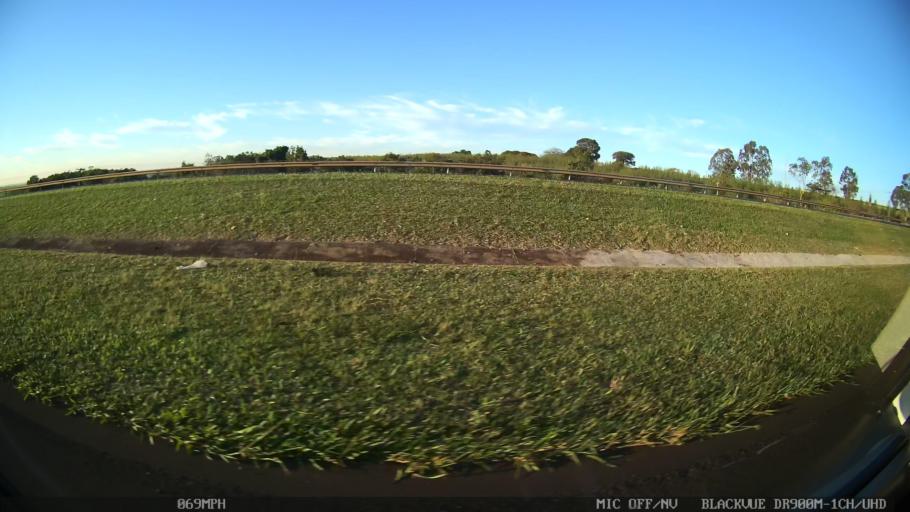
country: BR
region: Sao Paulo
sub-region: Ibate
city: Ibate
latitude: -21.9178
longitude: -48.0386
